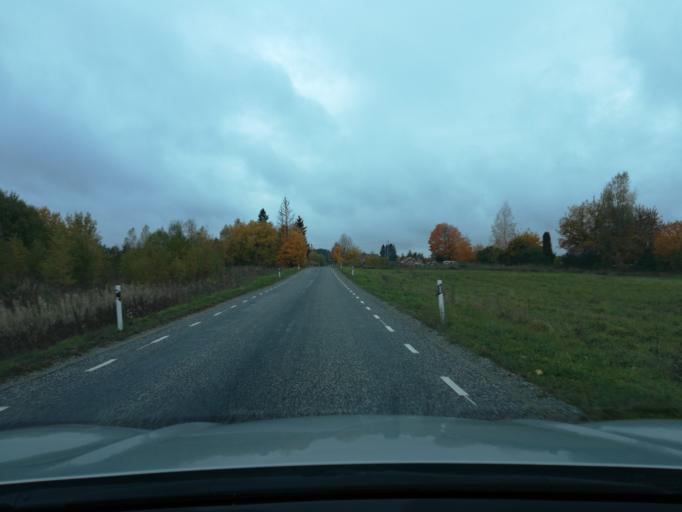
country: EE
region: Ida-Virumaa
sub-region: Johvi vald
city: Johvi
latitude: 59.1495
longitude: 27.3754
